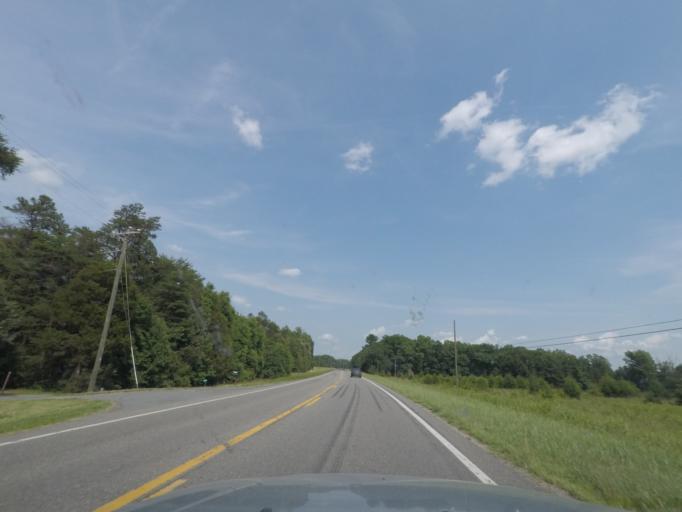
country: US
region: Virginia
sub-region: Fluvanna County
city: Palmyra
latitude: 37.8160
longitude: -78.2576
